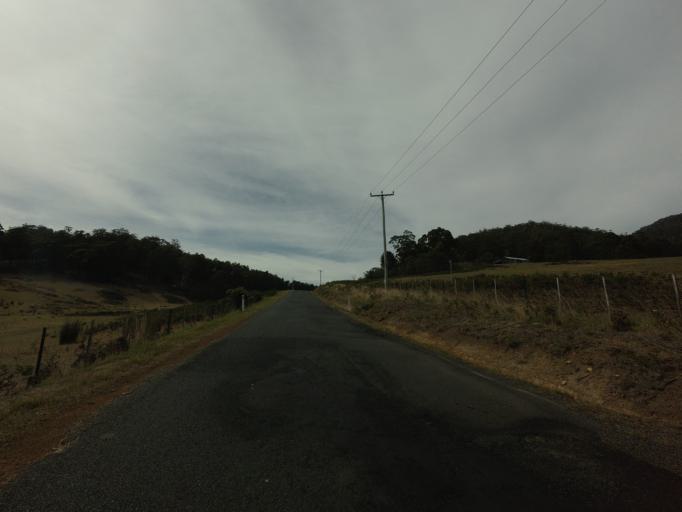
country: AU
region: Tasmania
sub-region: Sorell
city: Sorell
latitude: -42.4402
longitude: 147.5345
